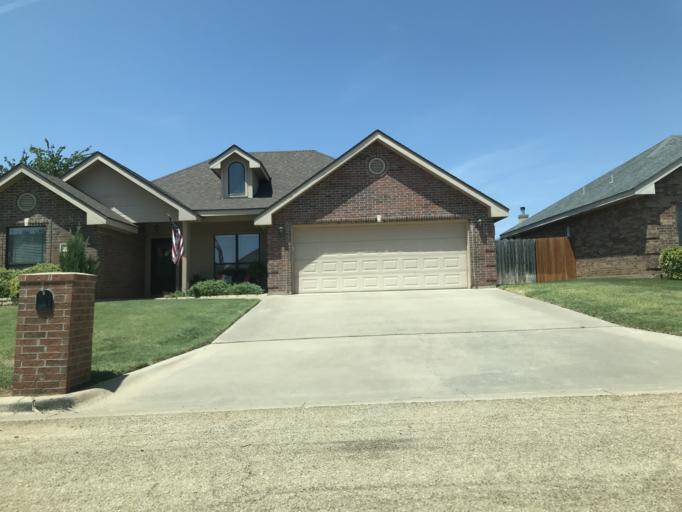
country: US
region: Texas
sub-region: Taylor County
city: Abilene
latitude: 32.4902
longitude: -99.6883
